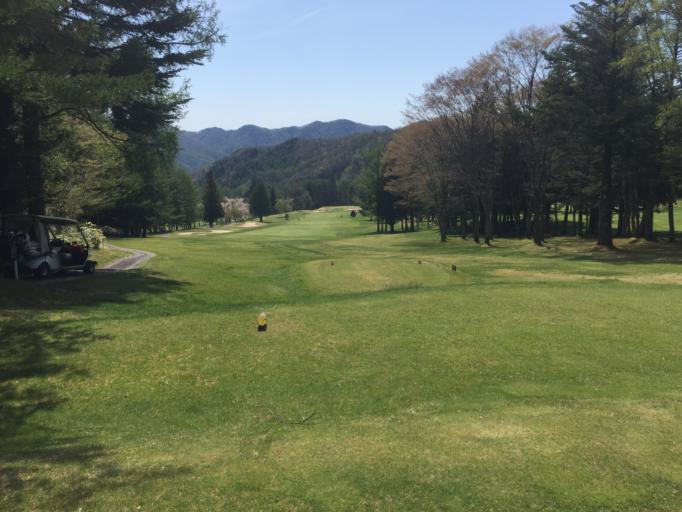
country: JP
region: Gifu
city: Nakatsugawa
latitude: 35.4084
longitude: 137.6693
